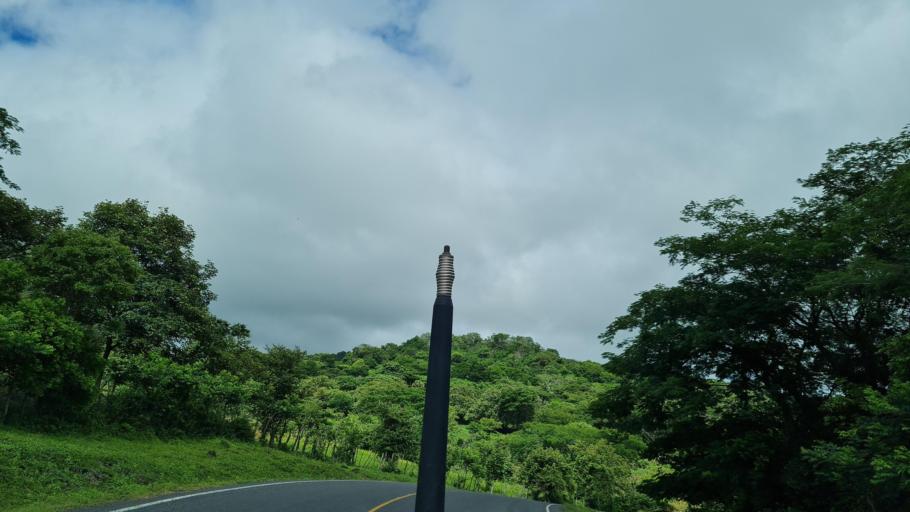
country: NI
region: Matagalpa
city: Terrabona
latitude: 12.5915
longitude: -85.9169
